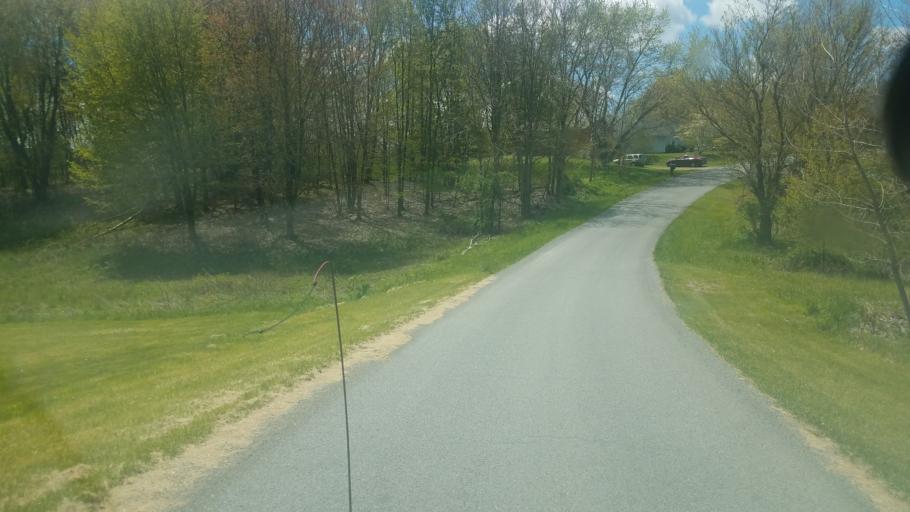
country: US
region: Ohio
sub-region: Knox County
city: Gambier
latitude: 40.4208
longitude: -82.3550
